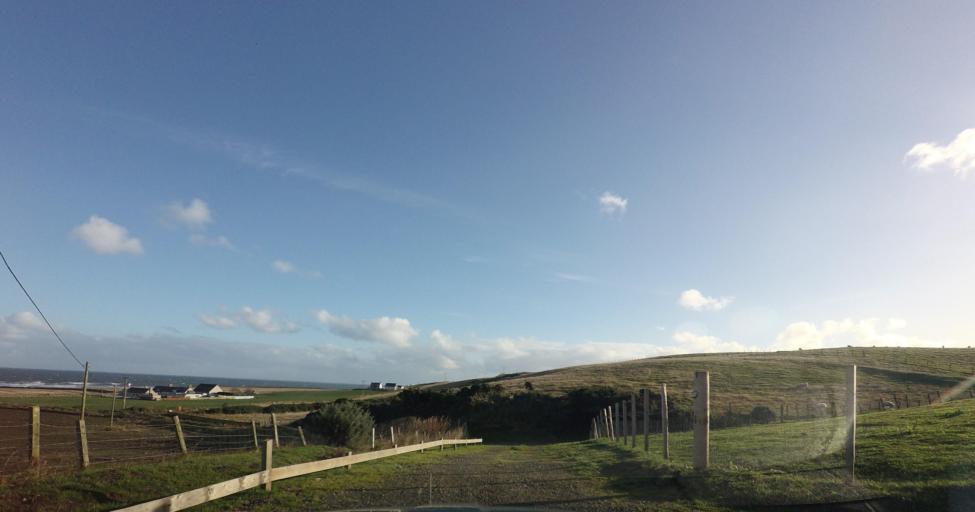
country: GB
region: Scotland
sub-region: Aberdeenshire
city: Banff
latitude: 57.6649
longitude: -2.5535
